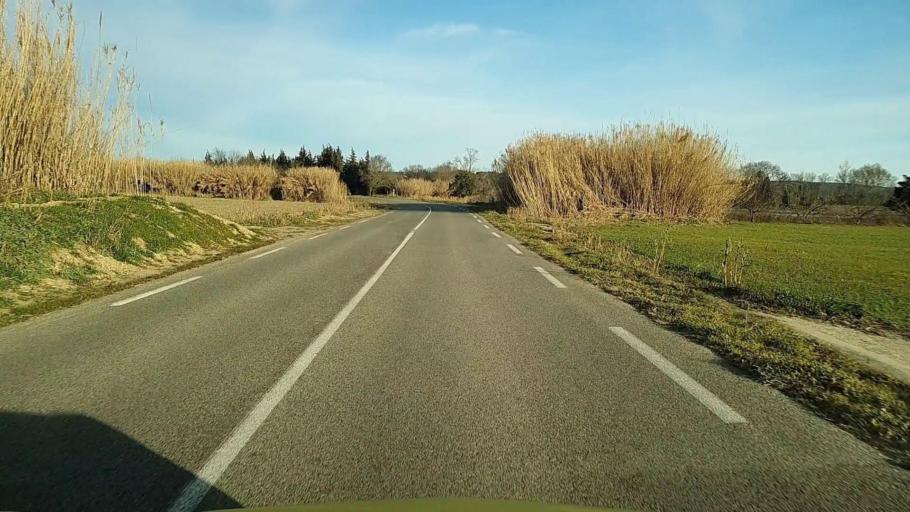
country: FR
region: Languedoc-Roussillon
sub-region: Departement du Gard
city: Remoulins
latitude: 43.9490
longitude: 4.5589
